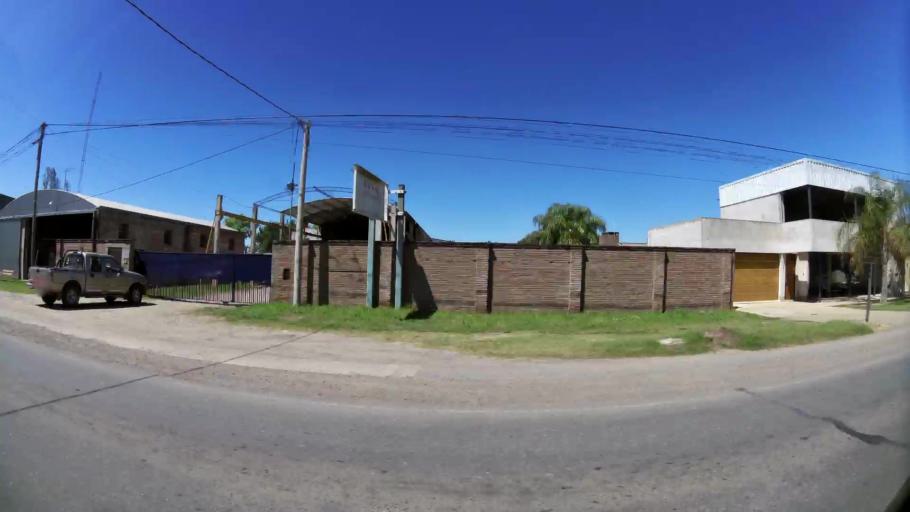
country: AR
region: Santa Fe
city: Esperanza
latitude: -31.4392
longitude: -60.9441
